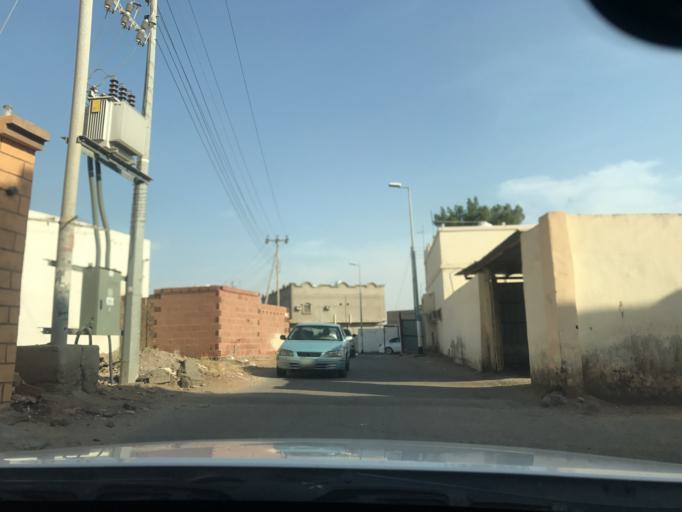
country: SA
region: Makkah
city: Al Jumum
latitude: 21.4444
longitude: 39.5343
